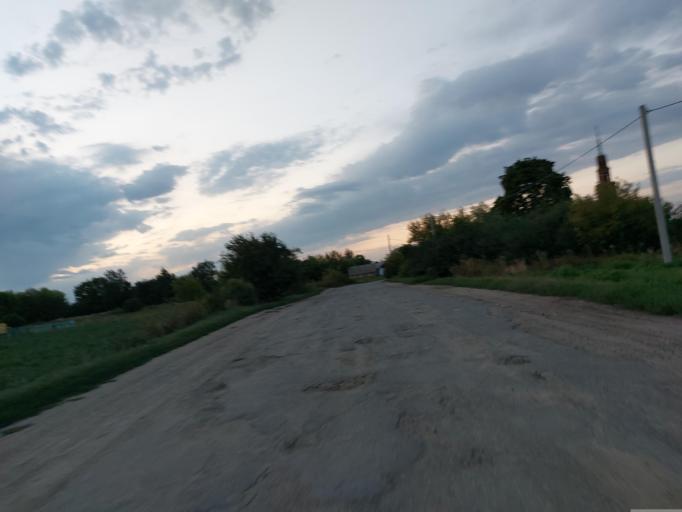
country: RU
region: Lipetsk
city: Dolgorukovo
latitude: 52.3752
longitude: 38.0520
